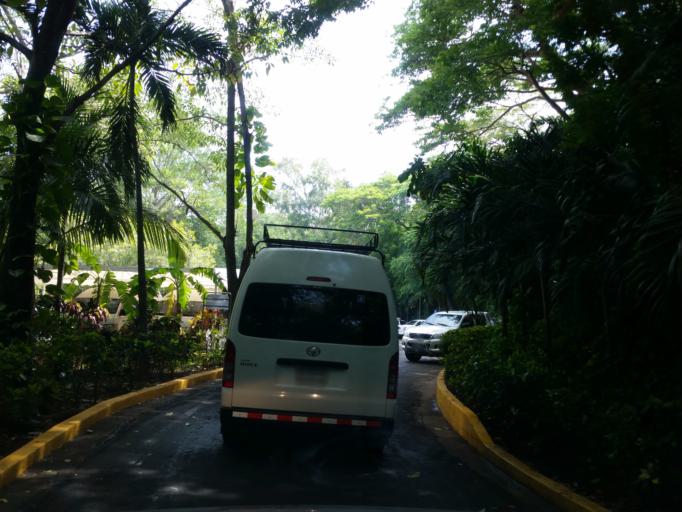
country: NI
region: Managua
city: Masachapa
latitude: 11.8073
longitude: -86.5181
